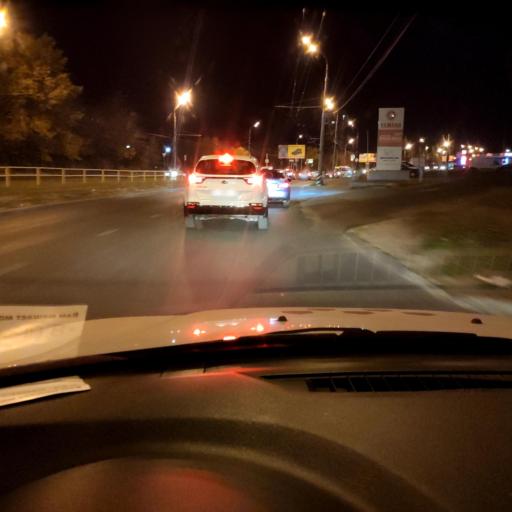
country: RU
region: Samara
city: Tol'yatti
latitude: 53.5072
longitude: 49.2546
